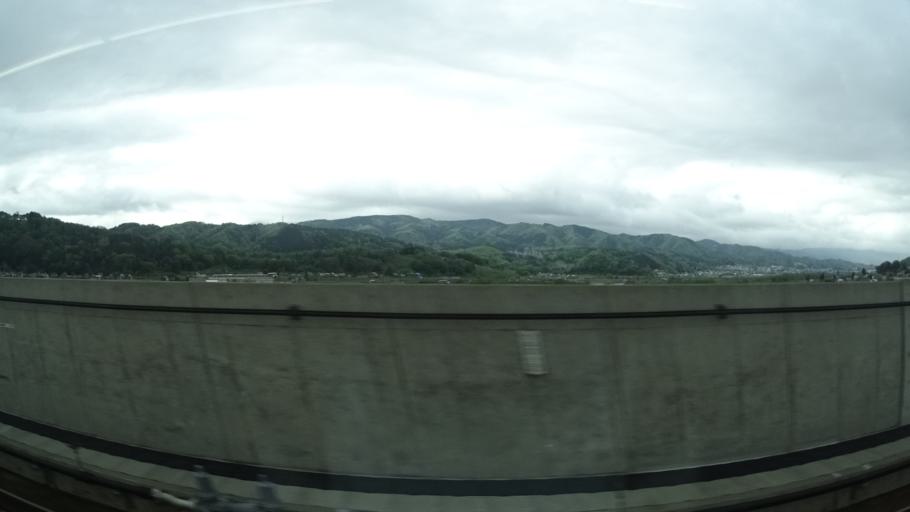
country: JP
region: Nagano
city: Nakano
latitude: 36.7918
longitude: 138.3616
